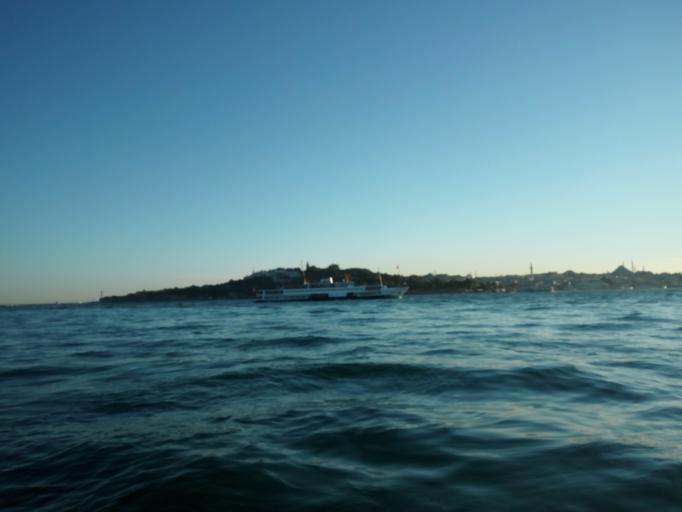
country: TR
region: Istanbul
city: Eminoenue
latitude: 41.0208
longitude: 28.9954
